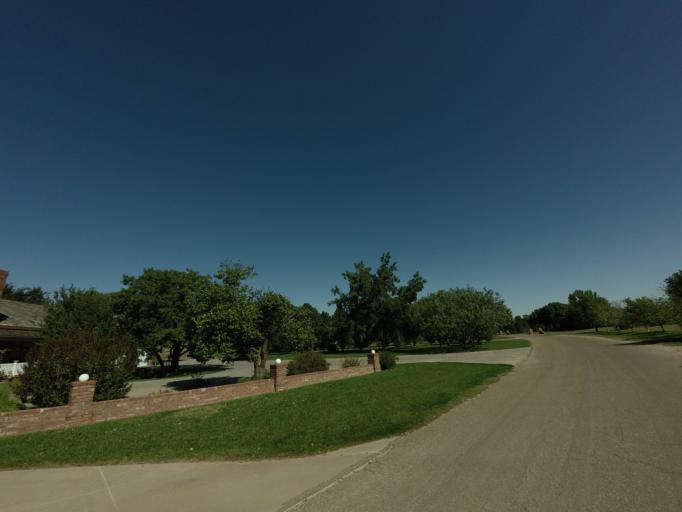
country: US
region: New Mexico
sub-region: Curry County
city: Clovis
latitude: 34.4280
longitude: -103.1684
